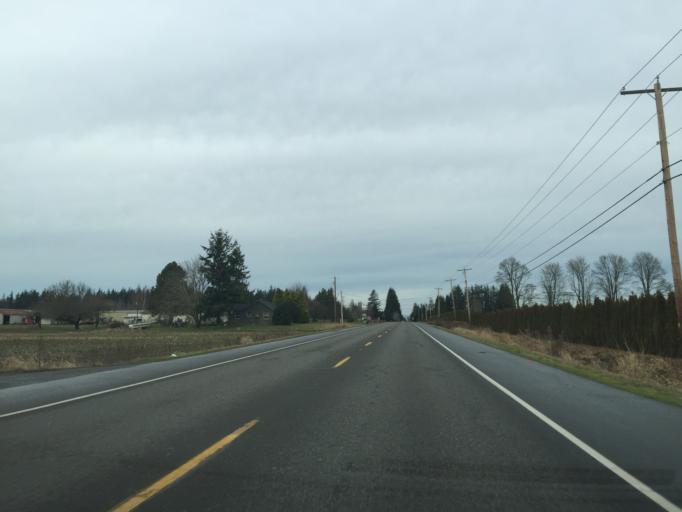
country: US
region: Washington
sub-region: Whatcom County
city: Ferndale
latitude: 48.8647
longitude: -122.5409
